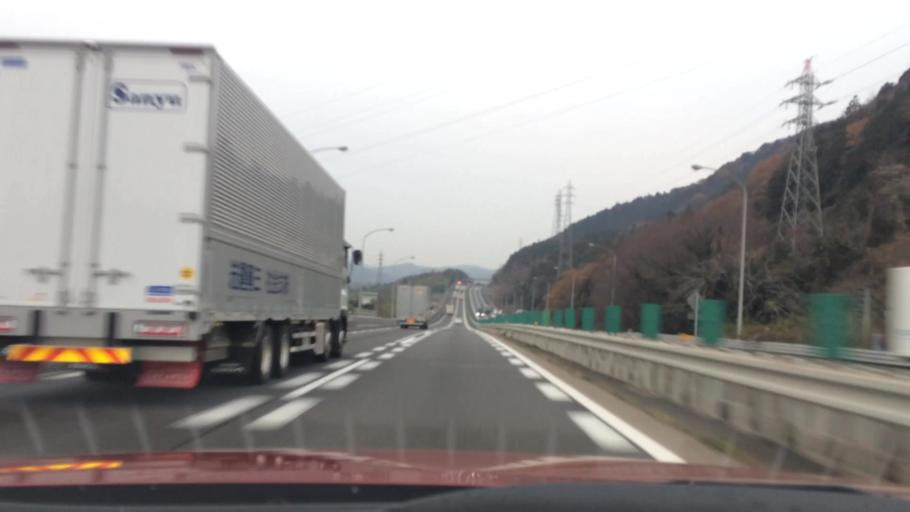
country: JP
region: Gifu
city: Tarui
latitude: 35.3349
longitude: 136.5225
